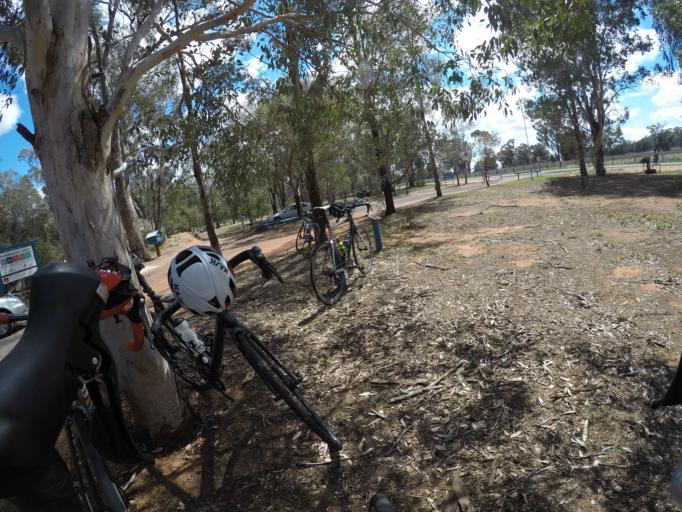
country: AU
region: New South Wales
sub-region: Dubbo Municipality
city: Dubbo
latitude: -32.4882
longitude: 148.5555
